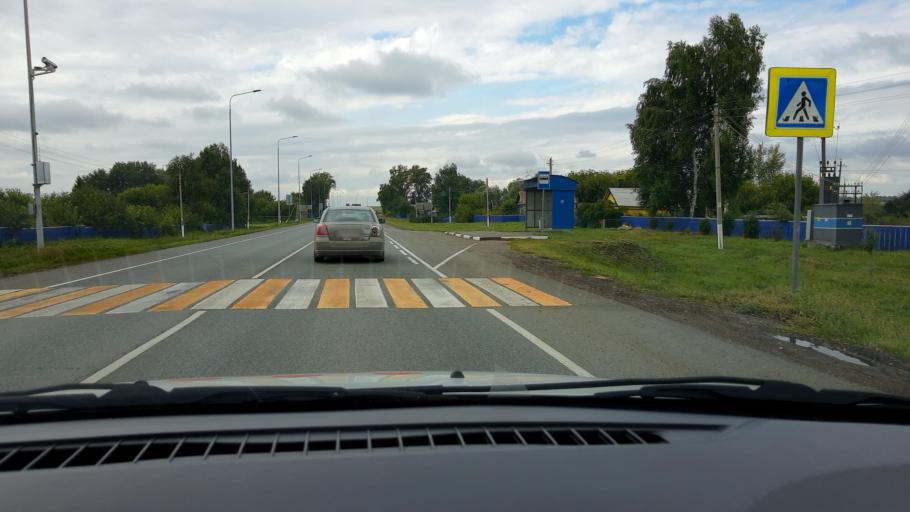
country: RU
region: Tatarstan
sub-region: Alekseyevskiy Rayon
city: Alekseyevskoye
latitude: 55.3100
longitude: 50.3021
